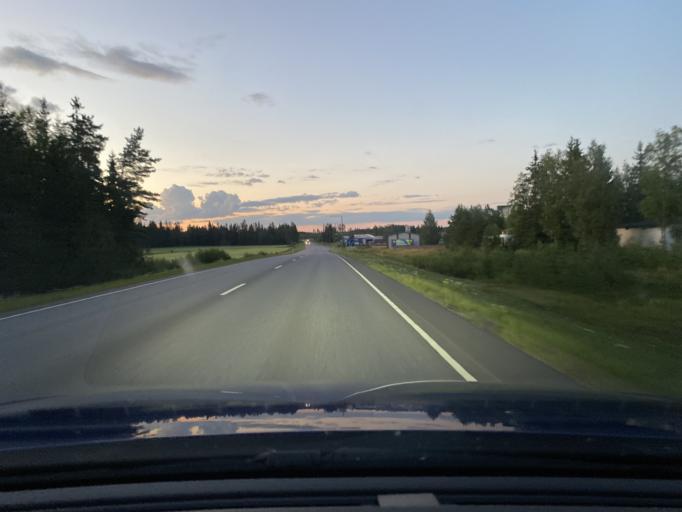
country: FI
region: Varsinais-Suomi
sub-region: Loimaa
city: Poeytyae
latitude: 60.7464
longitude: 22.6056
